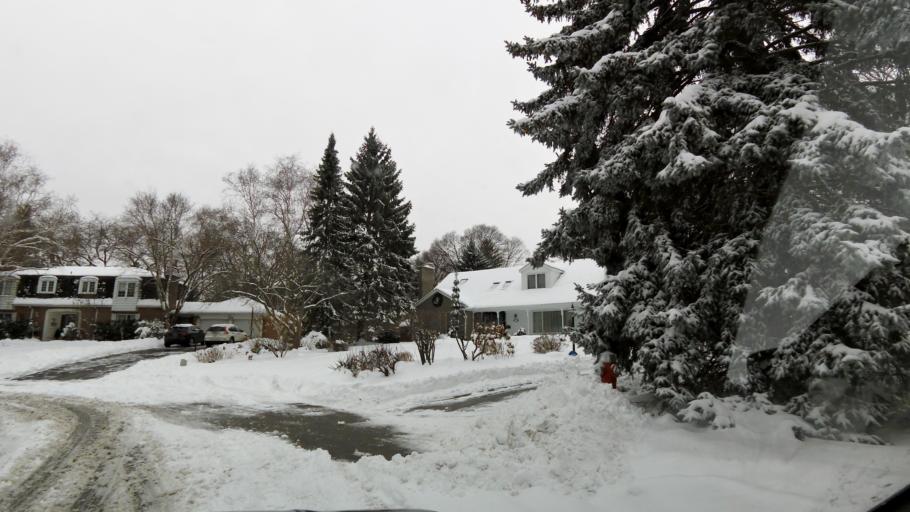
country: CA
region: Ontario
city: Mississauga
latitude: 43.5529
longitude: -79.6086
